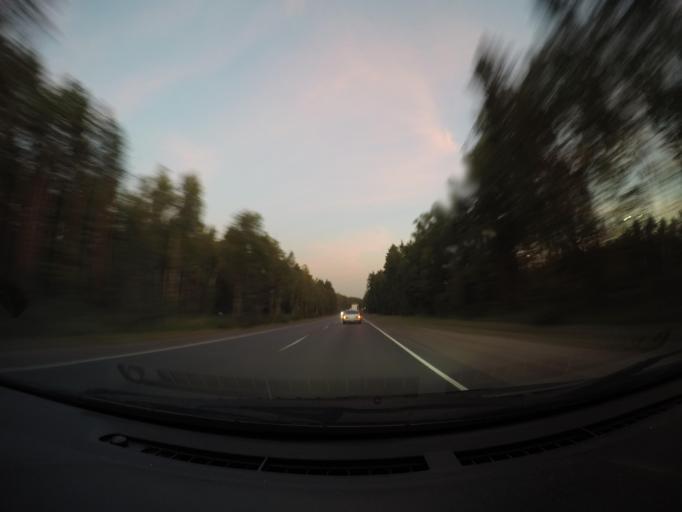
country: RU
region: Moskovskaya
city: Gzhel'
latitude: 55.5443
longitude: 38.4037
